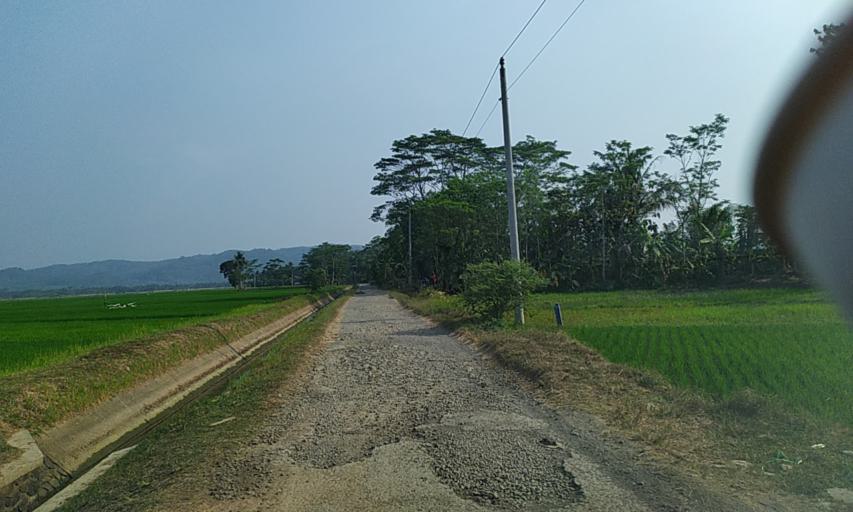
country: ID
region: Central Java
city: Mulyadadi
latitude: -7.3362
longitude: 108.7561
